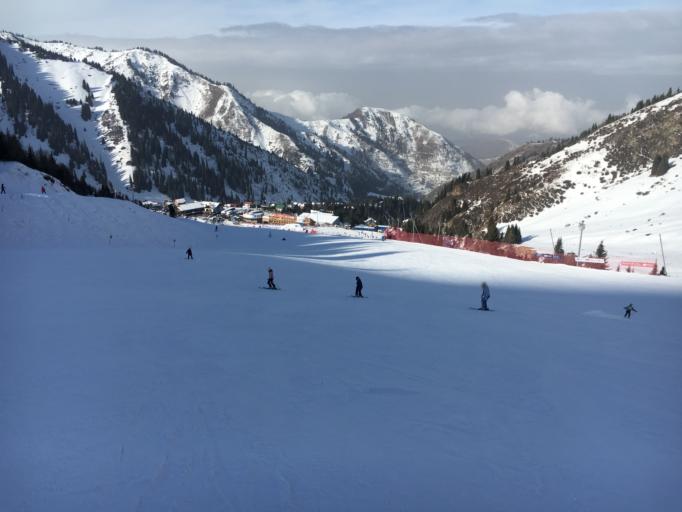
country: KZ
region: Almaty Qalasy
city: Almaty
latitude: 43.1247
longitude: 77.0903
